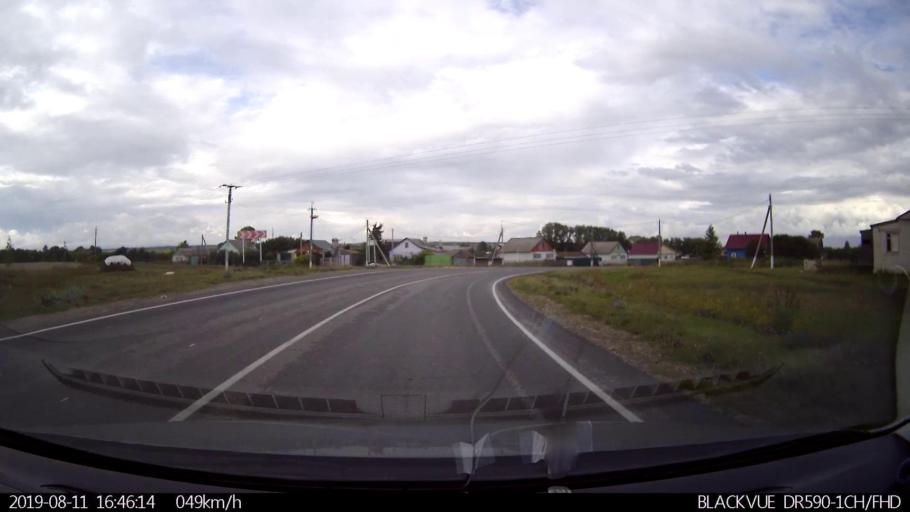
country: RU
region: Ulyanovsk
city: Mayna
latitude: 54.1968
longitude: 47.6870
